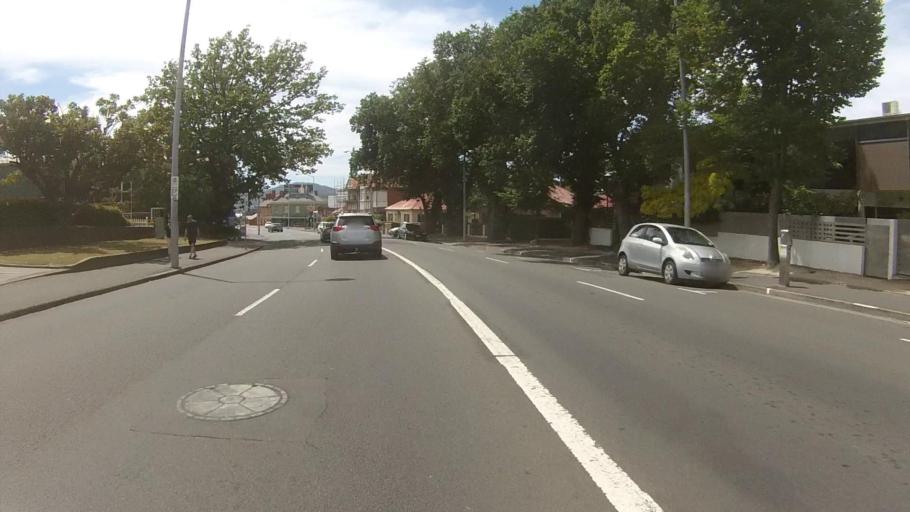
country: AU
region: Tasmania
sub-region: Hobart
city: Sandy Bay
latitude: -42.8905
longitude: 147.3295
